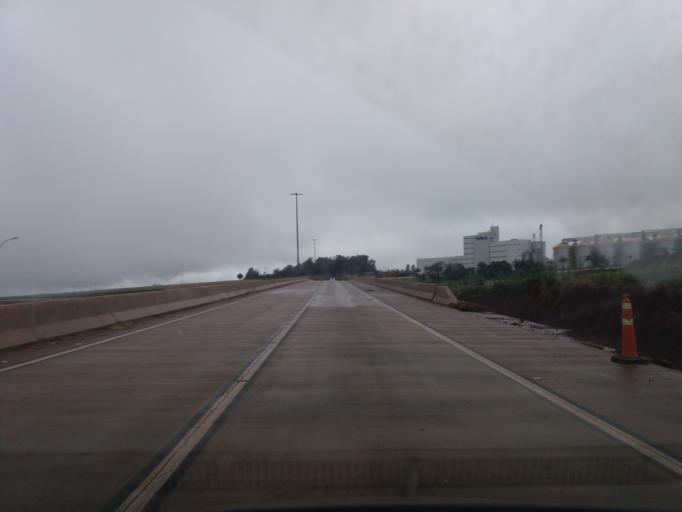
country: BR
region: Parana
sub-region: Cascavel
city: Cascavel
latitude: -25.1377
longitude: -53.5875
